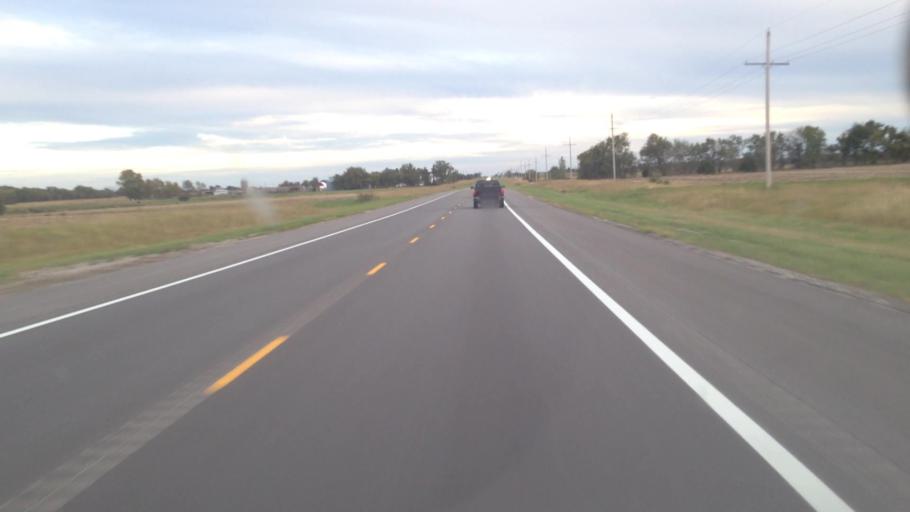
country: US
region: Kansas
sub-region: Franklin County
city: Ottawa
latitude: 38.5307
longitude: -95.2677
